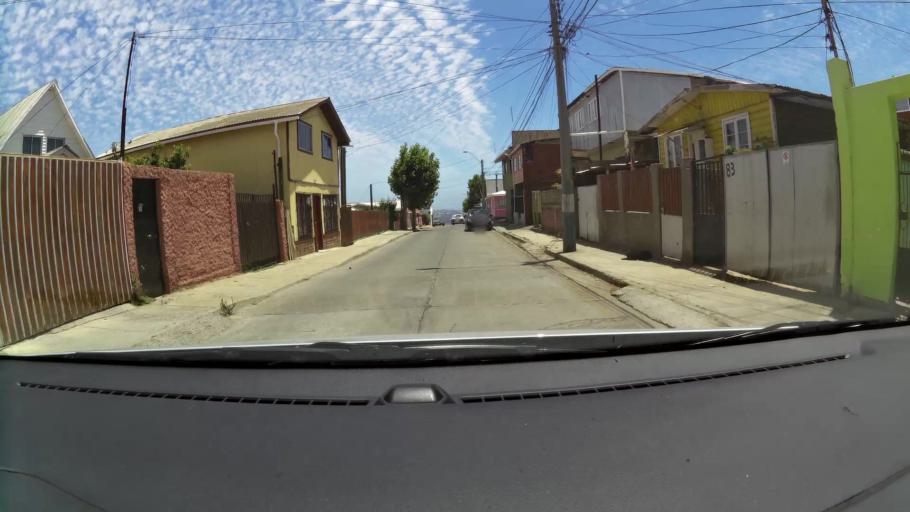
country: CL
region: Valparaiso
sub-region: Provincia de Valparaiso
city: Vina del Mar
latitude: -33.0484
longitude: -71.5822
